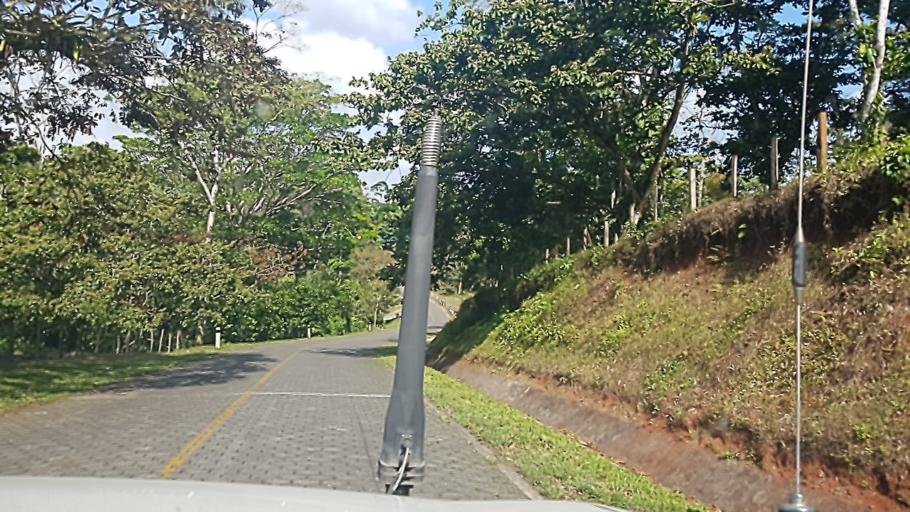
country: NI
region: Atlantico Sur
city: Nueva Guinea
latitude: 11.6981
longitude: -84.3949
